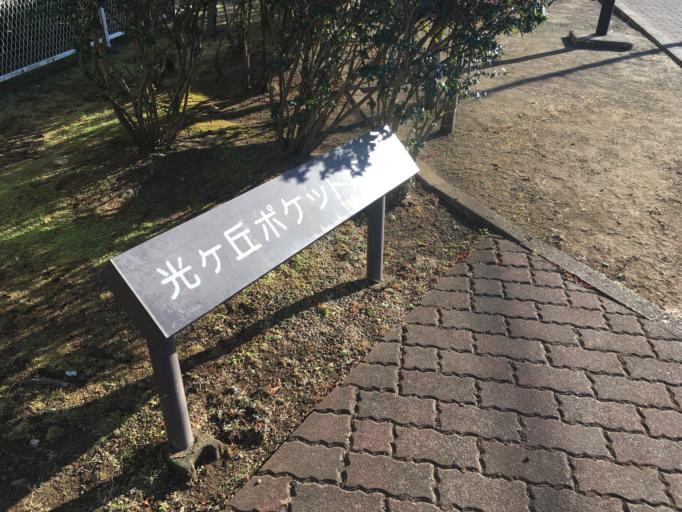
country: JP
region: Kanagawa
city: Minami-rinkan
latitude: 35.4607
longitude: 139.4692
